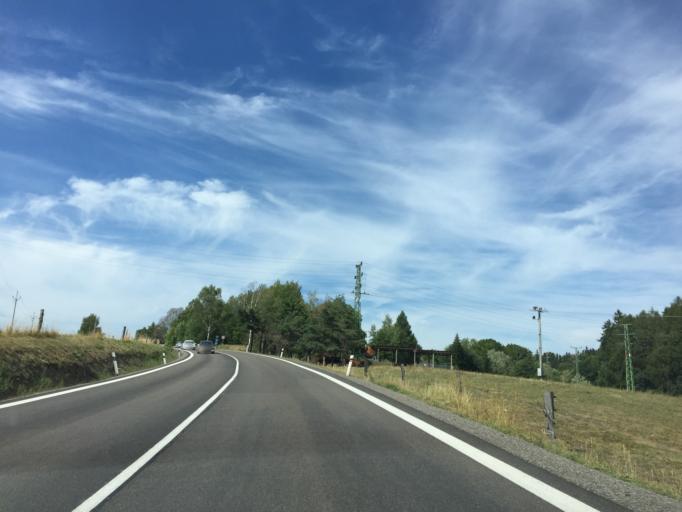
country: CZ
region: Central Bohemia
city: Votice
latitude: 49.5974
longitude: 14.6617
